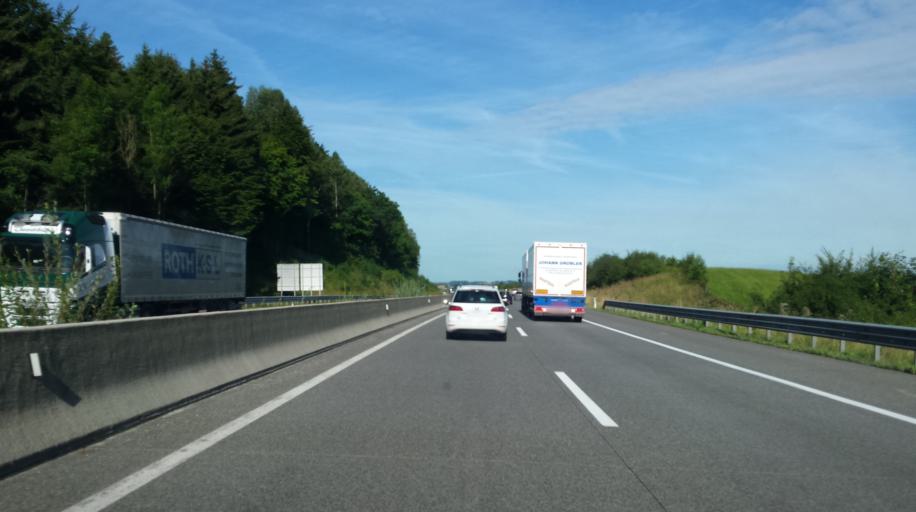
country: AT
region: Upper Austria
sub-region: Politischer Bezirk Vocklabruck
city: Aurach am Hongar
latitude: 47.9504
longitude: 13.7060
